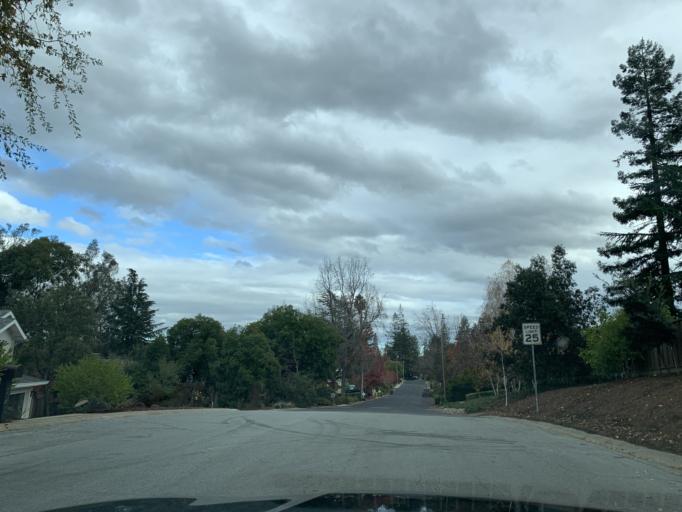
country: US
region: California
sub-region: Santa Clara County
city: Monte Sereno
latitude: 37.2579
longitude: -121.9736
